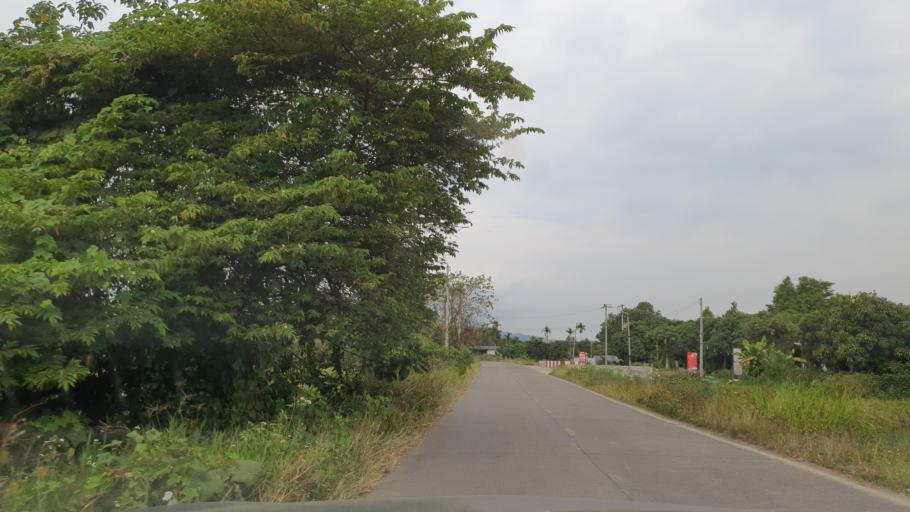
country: TH
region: Chiang Mai
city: Hang Dong
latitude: 18.6842
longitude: 98.9384
